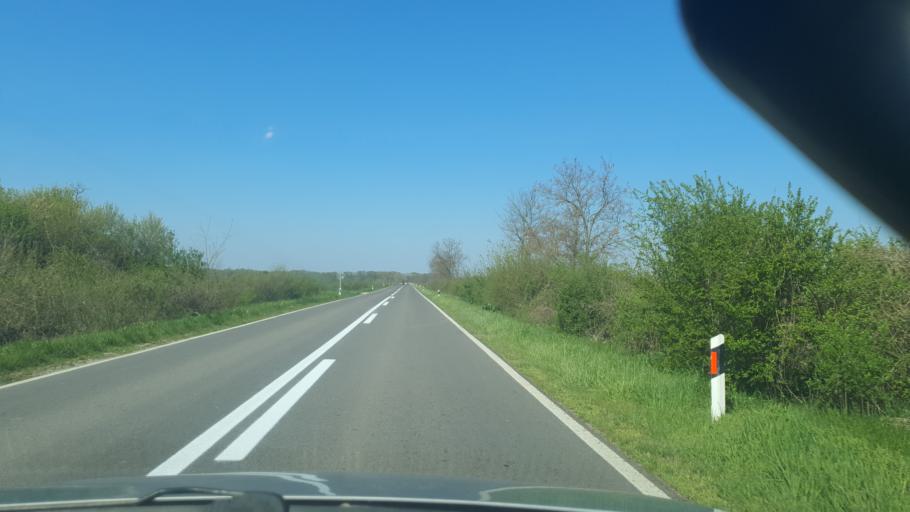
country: RS
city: Kolut
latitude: 45.8398
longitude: 18.9803
